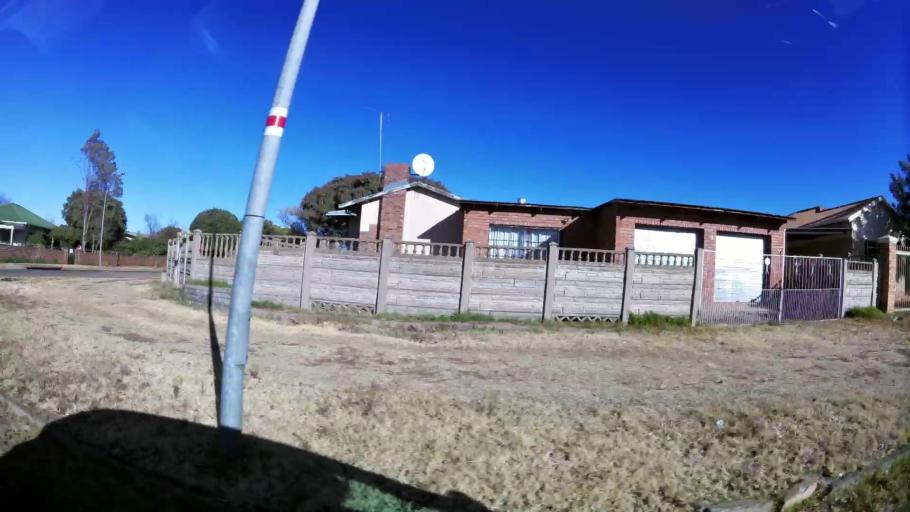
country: ZA
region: Northern Cape
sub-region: Frances Baard District Municipality
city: Kimberley
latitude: -28.7507
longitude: 24.7902
